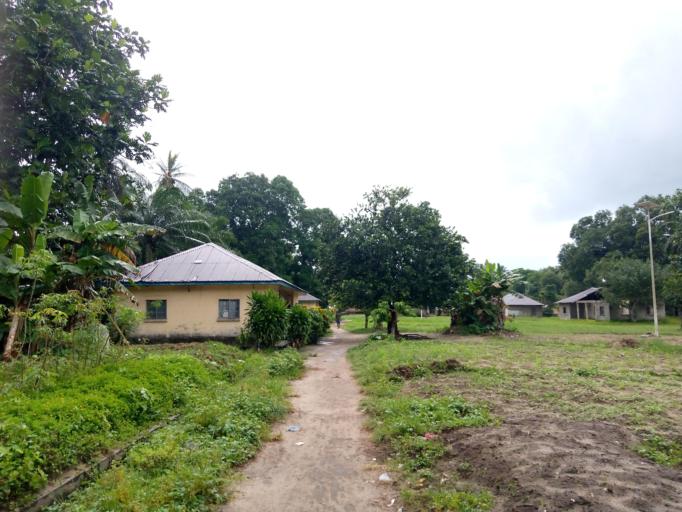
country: SL
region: Southern Province
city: Bonthe
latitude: 7.5321
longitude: -12.5089
